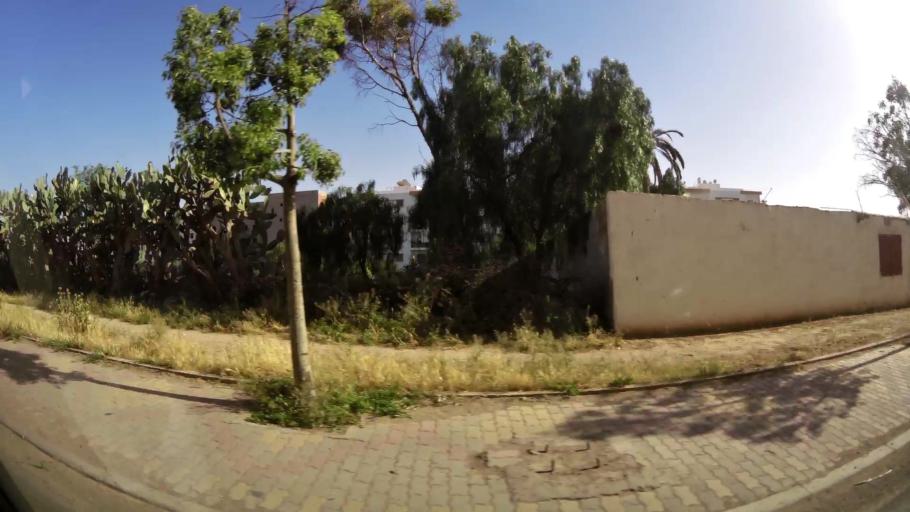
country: MA
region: Souss-Massa-Draa
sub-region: Inezgane-Ait Mellou
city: Inezgane
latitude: 30.3722
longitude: -9.5205
